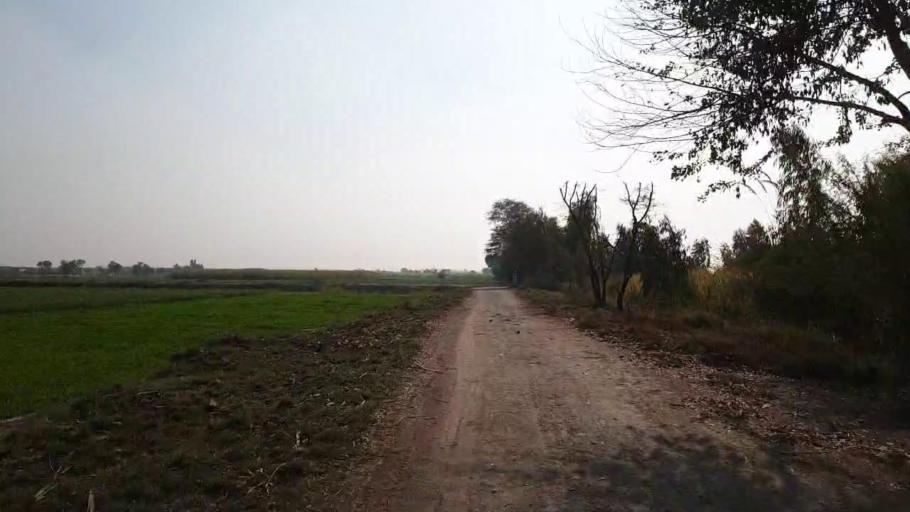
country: PK
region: Sindh
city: Tando Adam
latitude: 25.6632
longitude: 68.5717
